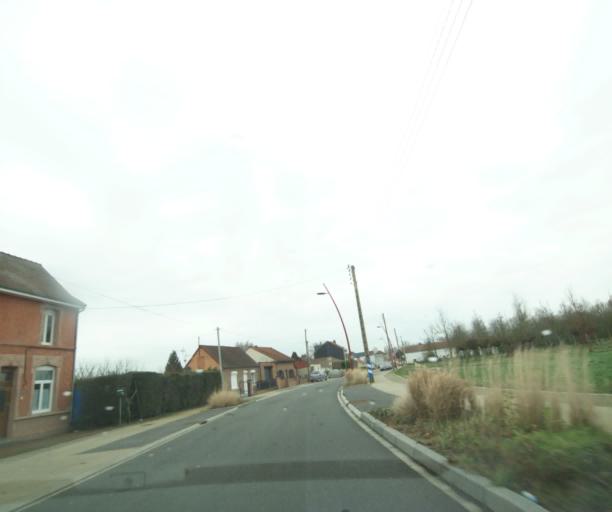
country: FR
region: Nord-Pas-de-Calais
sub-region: Departement du Nord
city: Vicq
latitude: 50.3991
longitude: 3.6117
